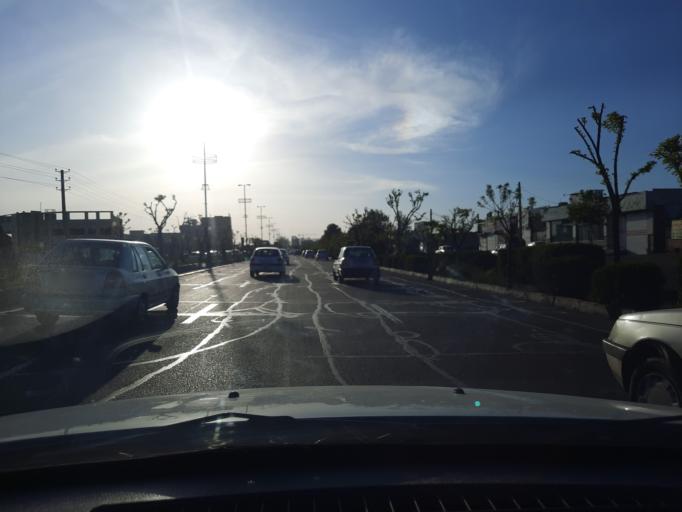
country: IR
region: Qazvin
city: Qazvin
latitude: 36.2645
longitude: 50.0377
